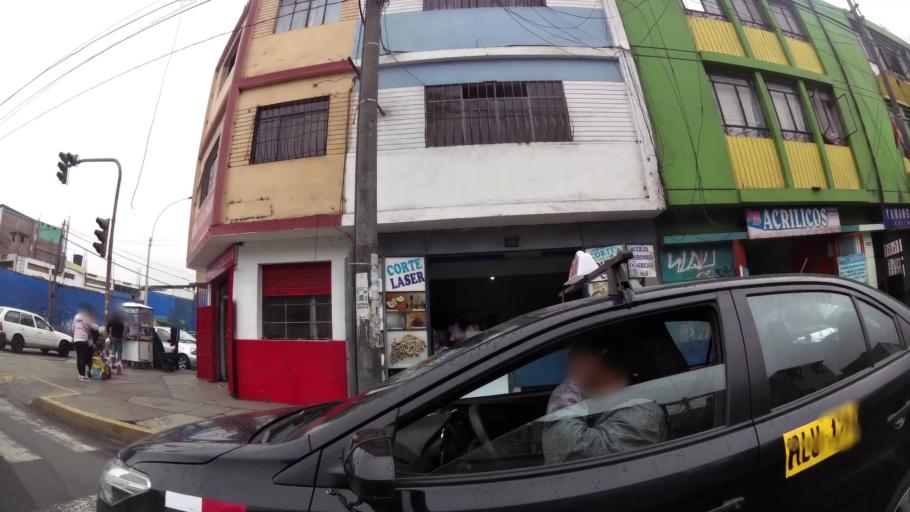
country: PE
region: Lima
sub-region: Lima
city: San Luis
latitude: -12.0689
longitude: -77.0181
